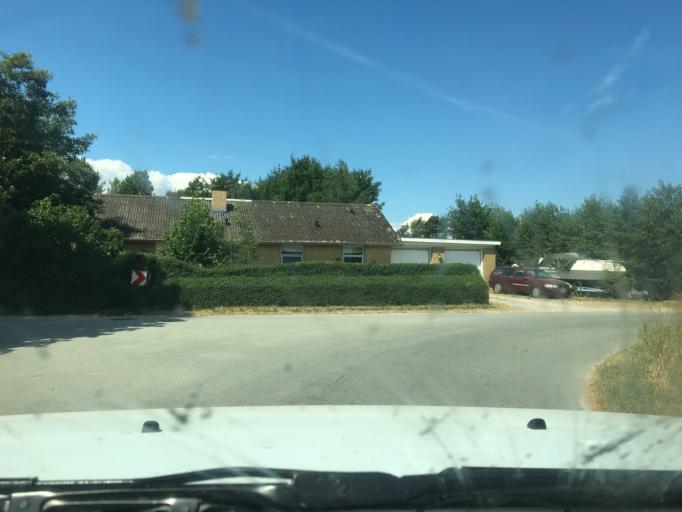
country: DK
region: Central Jutland
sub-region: Syddjurs Kommune
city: Hornslet
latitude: 56.3495
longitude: 10.2824
